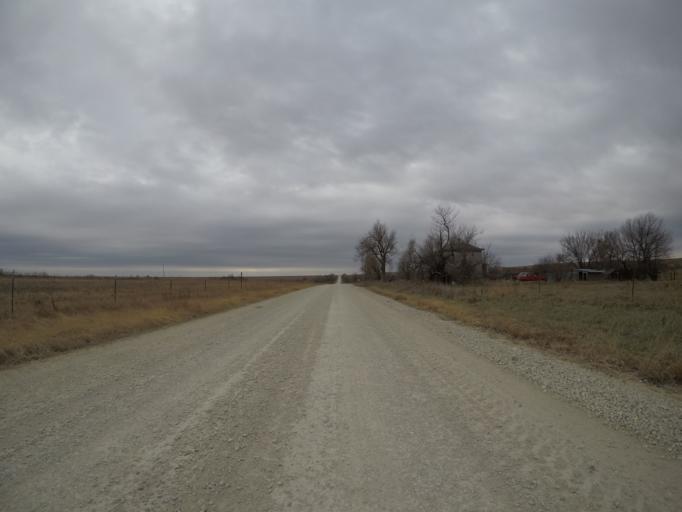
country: US
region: Kansas
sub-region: Wabaunsee County
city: Alma
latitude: 38.7748
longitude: -96.1498
